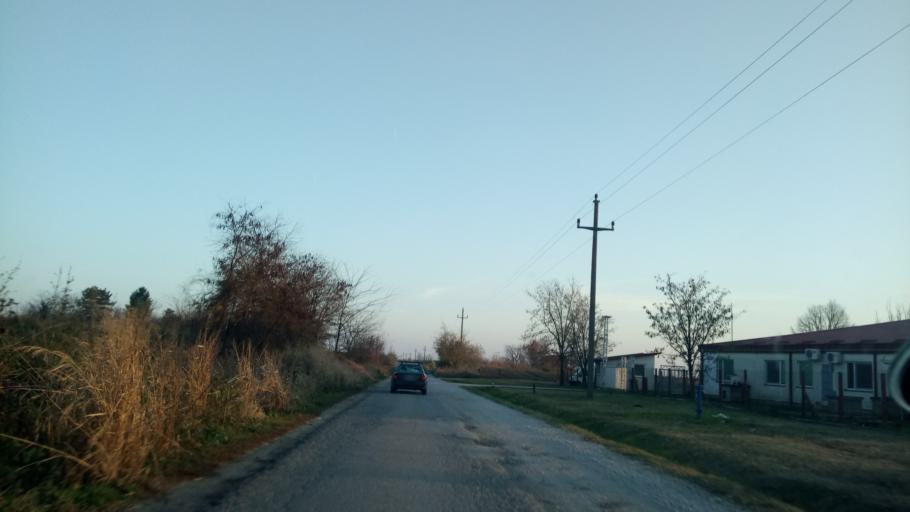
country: RS
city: Novi Slankamen
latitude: 45.1297
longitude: 20.2568
